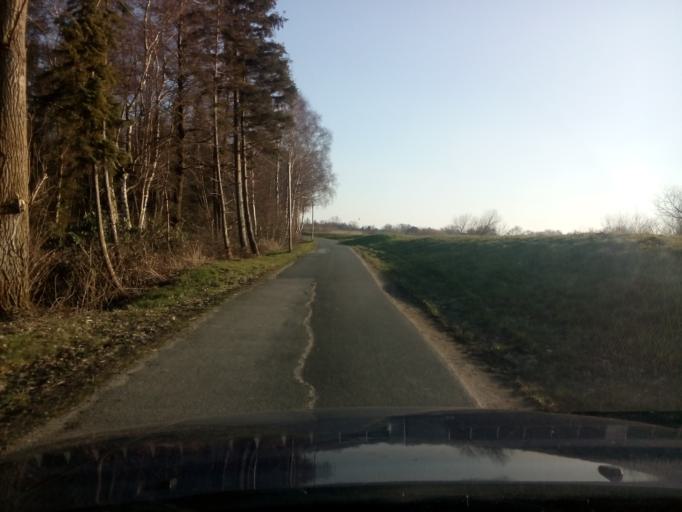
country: DE
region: Lower Saxony
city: Lilienthal
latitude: 53.1510
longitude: 8.8427
